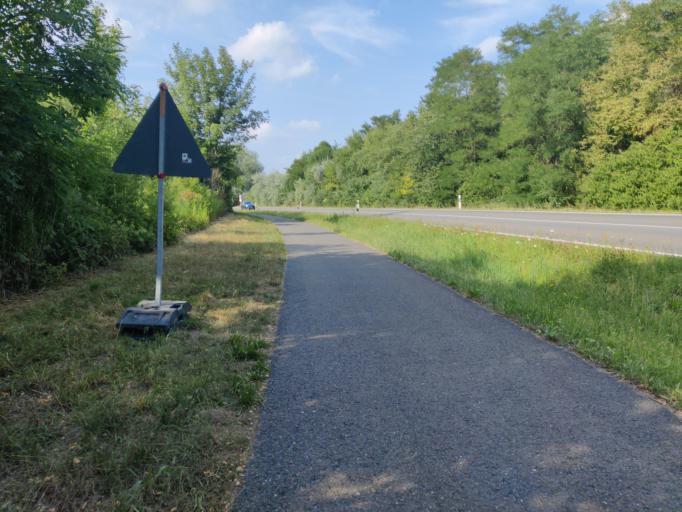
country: DE
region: Saxony
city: Deutzen
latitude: 51.1170
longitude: 12.4251
